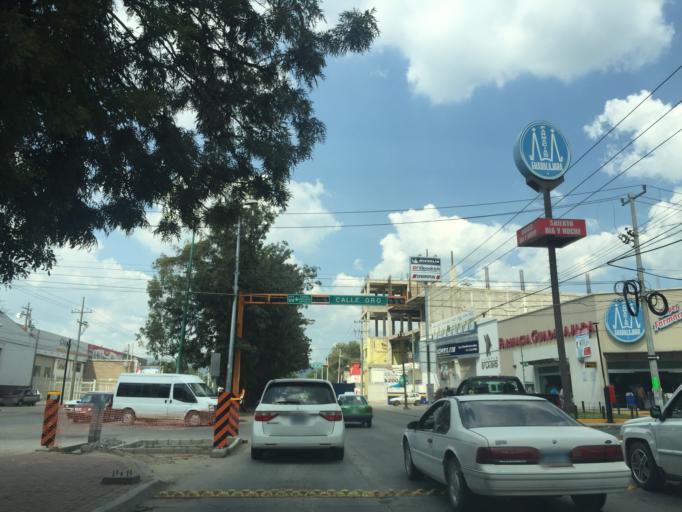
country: MX
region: Guanajuato
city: Leon
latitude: 21.1607
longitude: -101.6654
